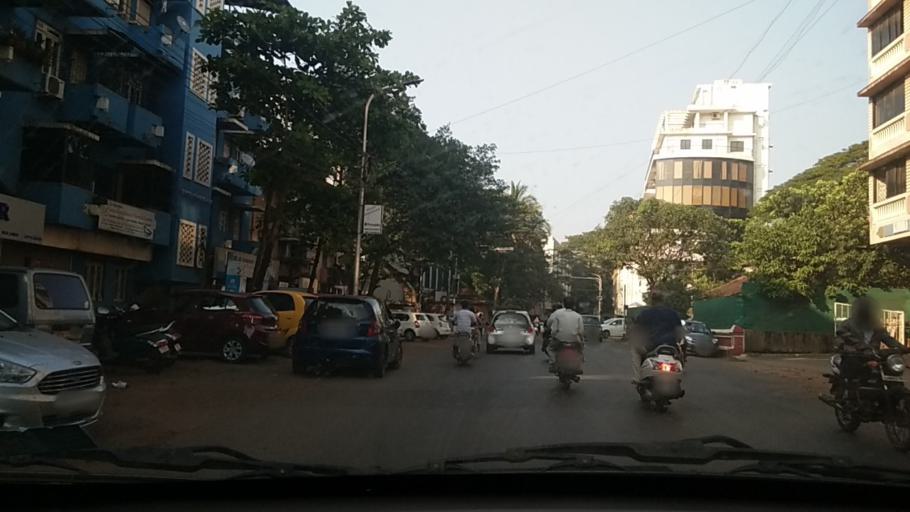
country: IN
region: Goa
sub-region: North Goa
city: Panaji
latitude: 15.4928
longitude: 73.8206
